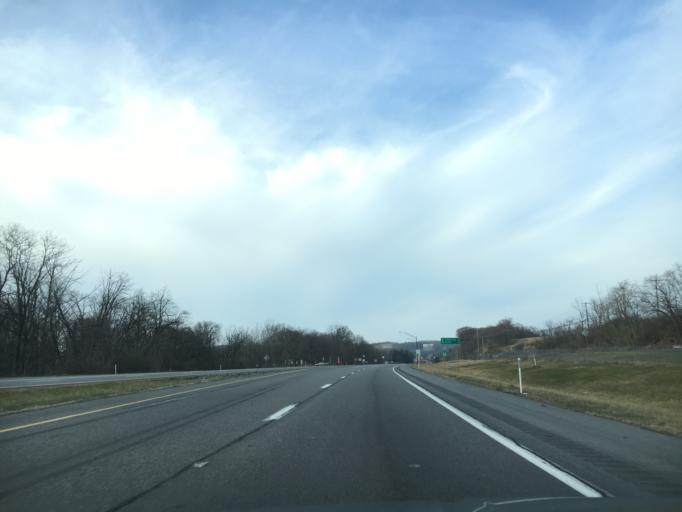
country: US
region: Pennsylvania
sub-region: Montour County
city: Danville
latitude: 40.9848
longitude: -76.6300
